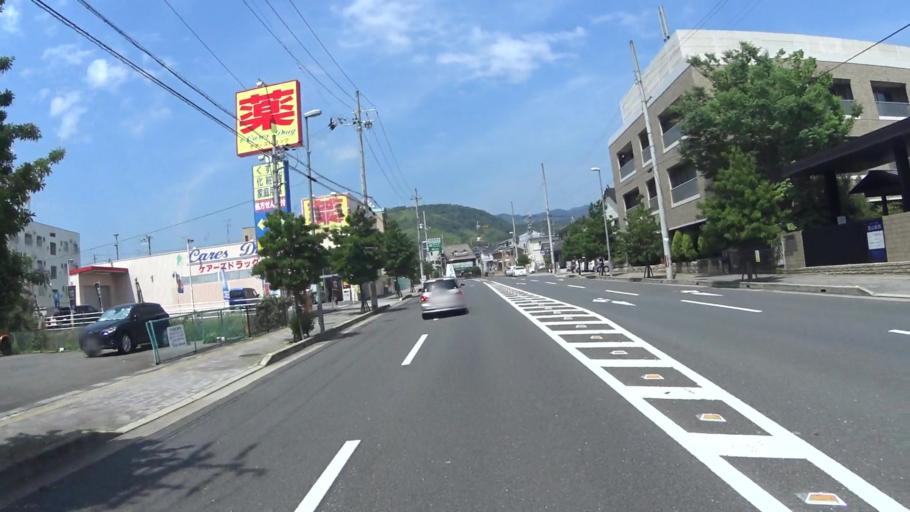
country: JP
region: Kyoto
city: Muko
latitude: 34.9288
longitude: 135.6908
